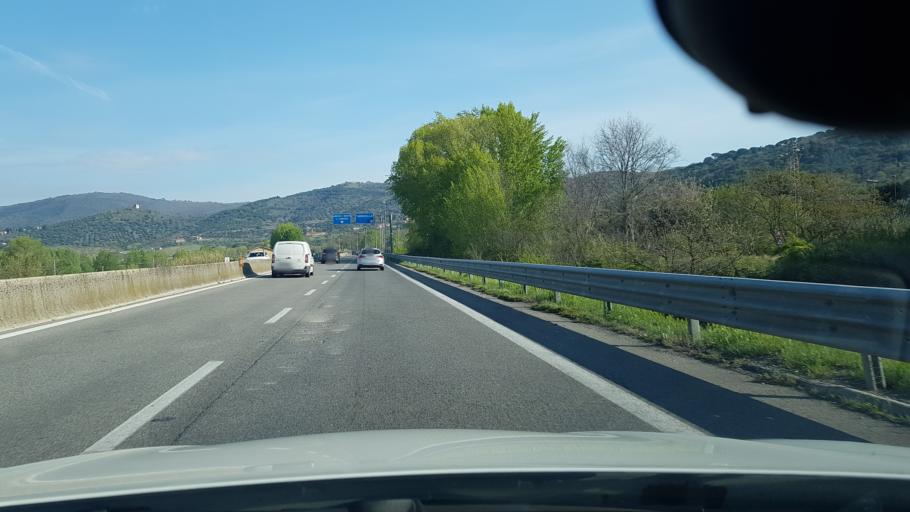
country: IT
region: Umbria
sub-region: Provincia di Perugia
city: Magione
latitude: 43.1653
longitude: 12.1893
